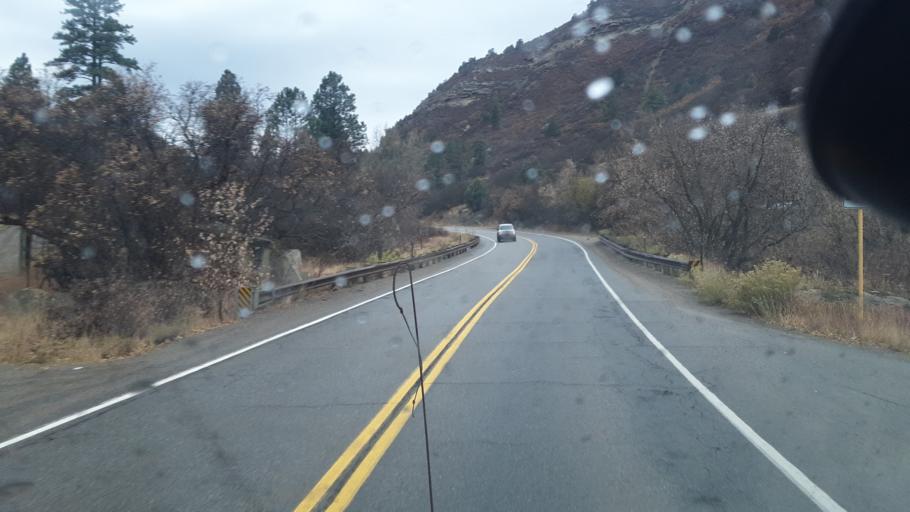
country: US
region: Colorado
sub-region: La Plata County
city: Durango
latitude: 37.2648
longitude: -107.9216
